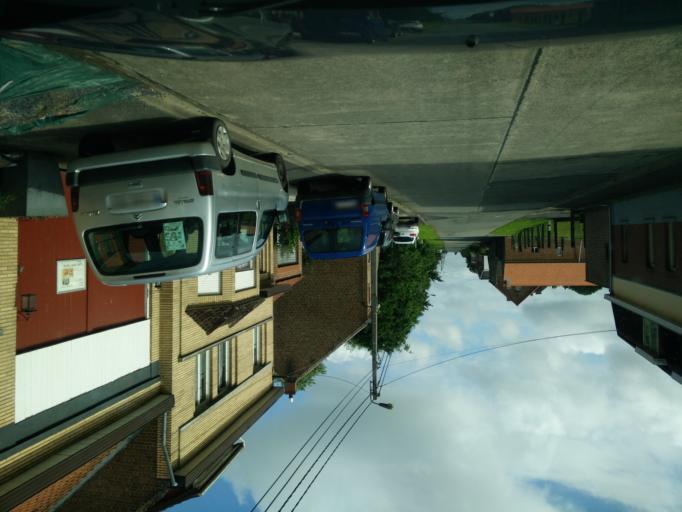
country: BE
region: Wallonia
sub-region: Province du Hainaut
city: Flobecq
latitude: 50.7647
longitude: 3.7307
